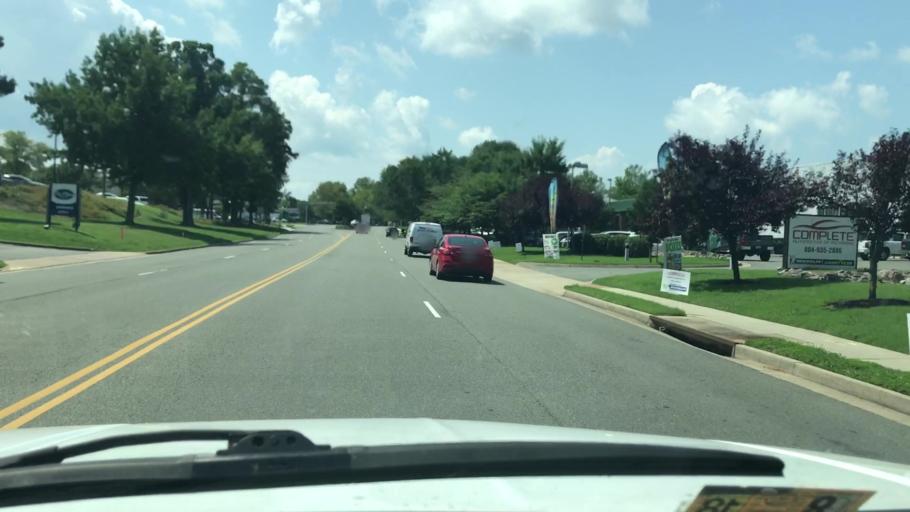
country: US
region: Virginia
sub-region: Henrico County
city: Short Pump
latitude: 37.6497
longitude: -77.5859
